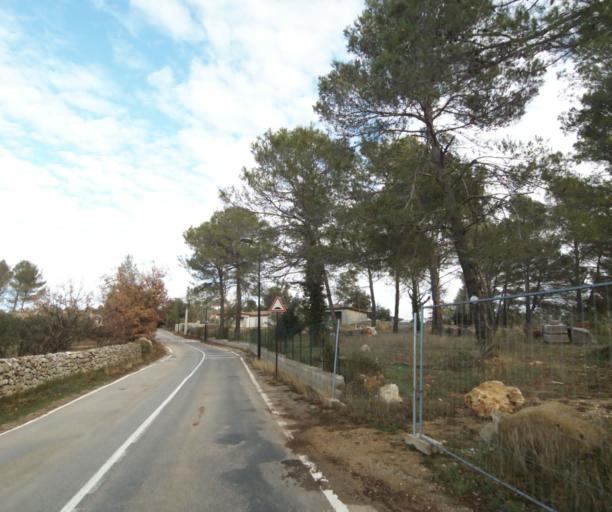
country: FR
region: Provence-Alpes-Cote d'Azur
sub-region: Departement du Var
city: Trans-en-Provence
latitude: 43.4906
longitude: 6.4836
